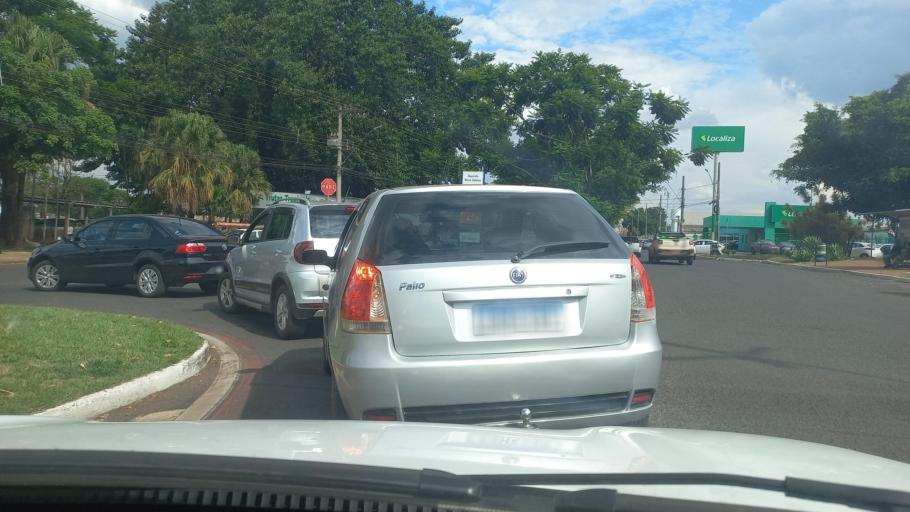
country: BR
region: Minas Gerais
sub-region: Uberaba
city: Uberaba
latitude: -19.7654
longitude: -47.9616
